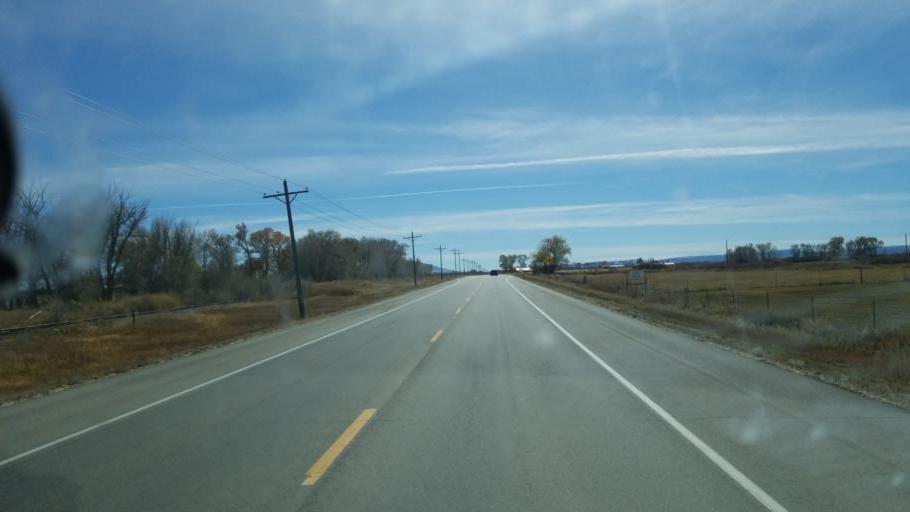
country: US
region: Colorado
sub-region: Conejos County
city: Conejos
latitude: 37.1397
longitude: -105.9970
